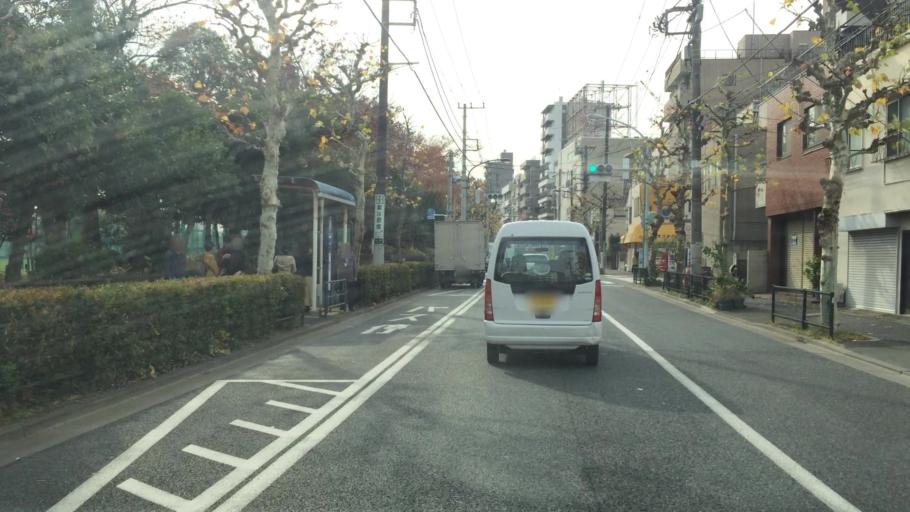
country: JP
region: Tokyo
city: Urayasu
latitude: 35.7203
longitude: 139.8062
